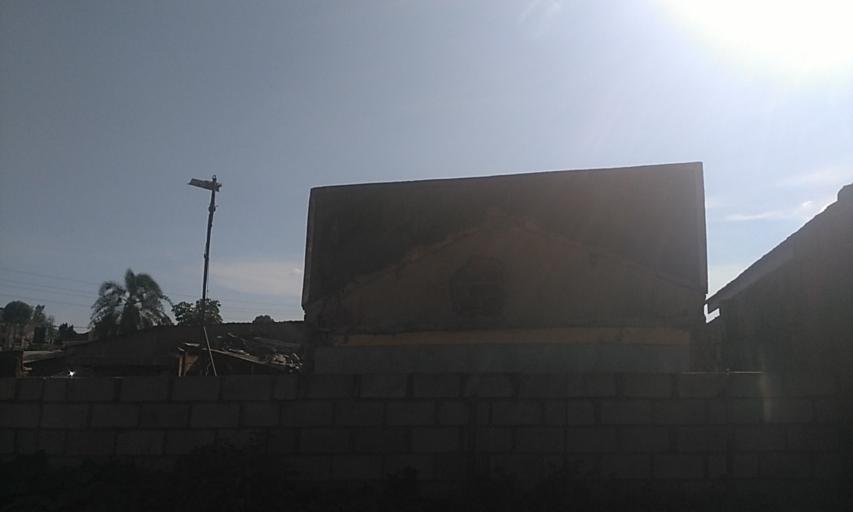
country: UG
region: Central Region
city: Kampala Central Division
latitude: 0.3276
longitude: 32.5353
